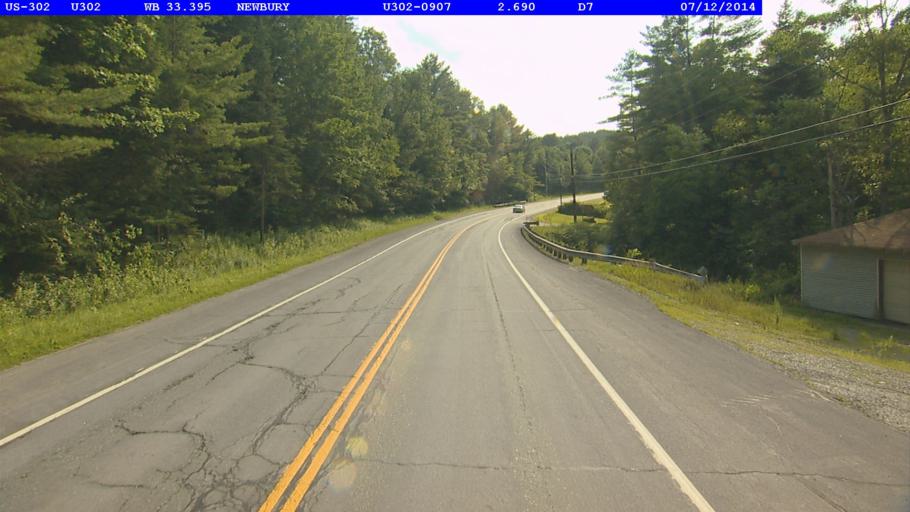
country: US
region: New Hampshire
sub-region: Grafton County
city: Woodsville
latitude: 44.1522
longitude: -72.0811
